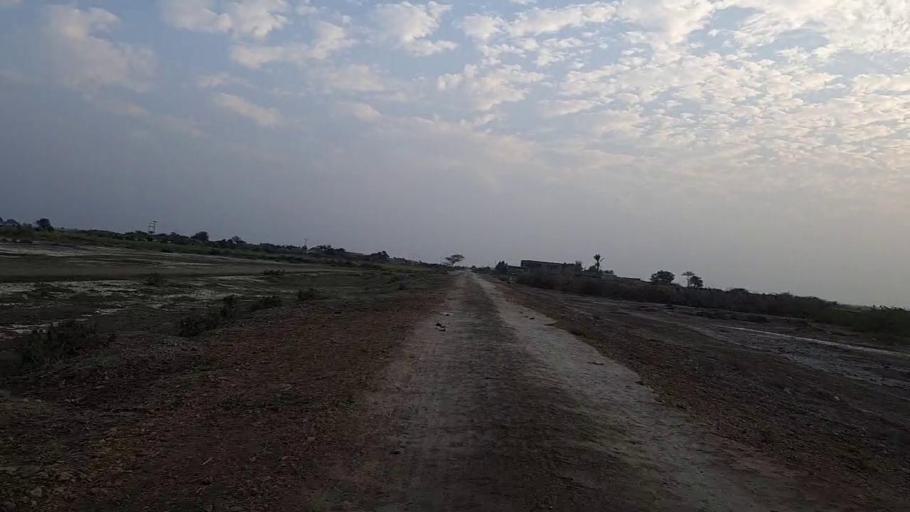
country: PK
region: Sindh
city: Pithoro
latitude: 25.4595
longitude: 69.3457
